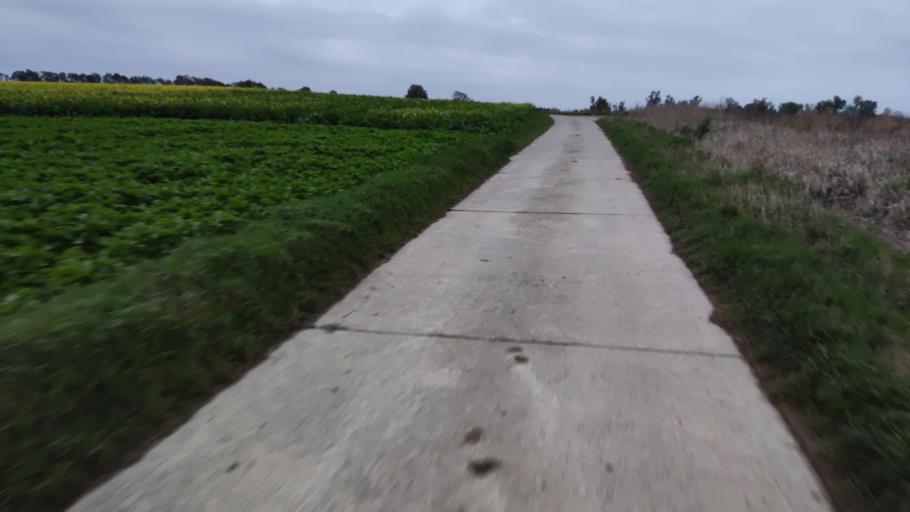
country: BE
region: Flanders
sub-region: Provincie Vlaams-Brabant
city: Tienen
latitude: 50.7792
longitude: 4.9307
